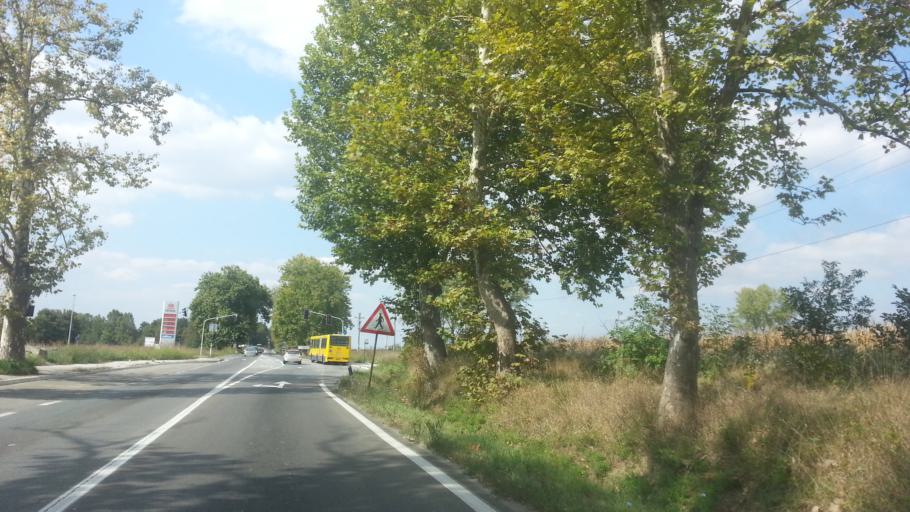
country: RS
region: Central Serbia
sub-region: Belgrade
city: Zemun
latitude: 44.8778
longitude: 20.3348
